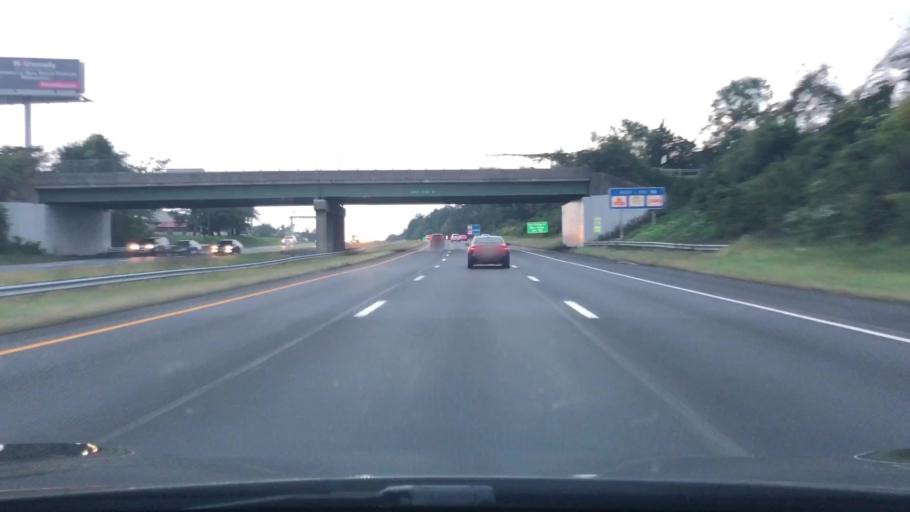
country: US
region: New Jersey
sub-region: Mercer County
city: Ewing
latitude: 40.2892
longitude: -74.7992
